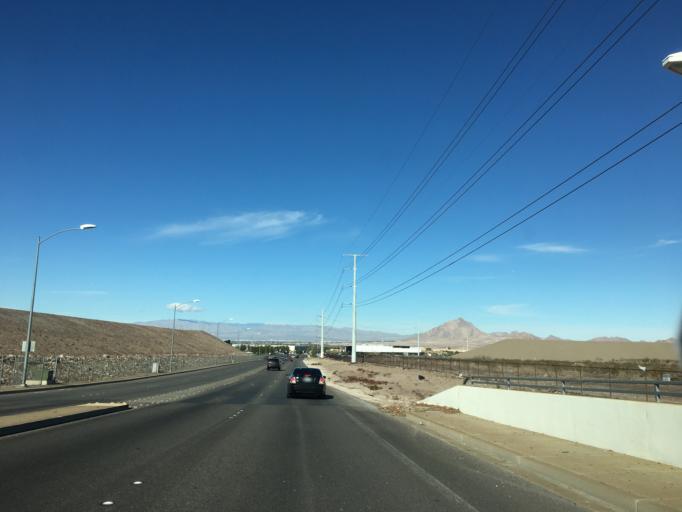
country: US
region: Nevada
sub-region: Clark County
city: Henderson
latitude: 36.0419
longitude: -115.0184
